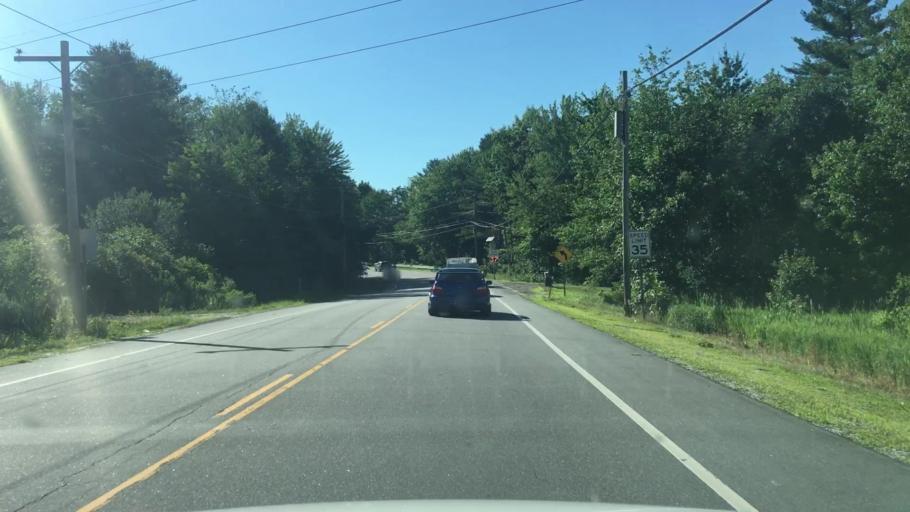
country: US
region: New Hampshire
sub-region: Rockingham County
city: Exeter
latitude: 43.0107
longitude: -71.0015
